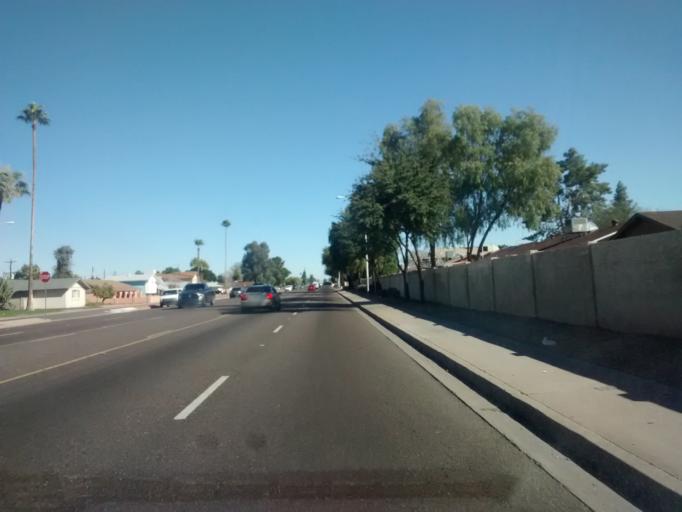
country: US
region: Arizona
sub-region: Maricopa County
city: Glendale
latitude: 33.5239
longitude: -112.1586
